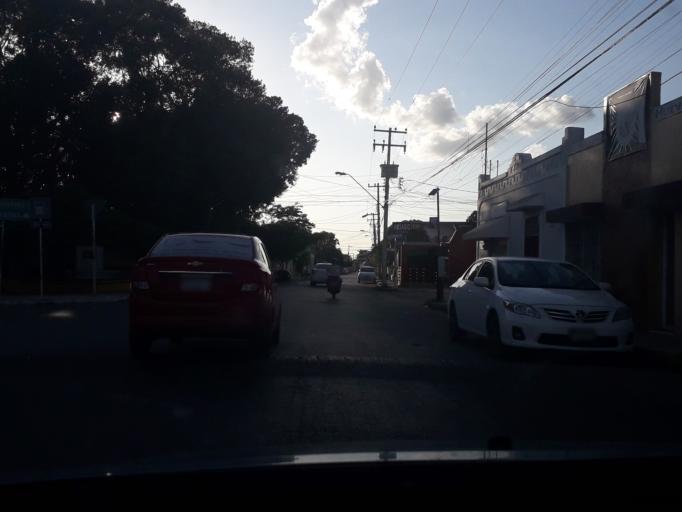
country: MX
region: Yucatan
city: Merida
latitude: 20.9664
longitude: -89.6448
